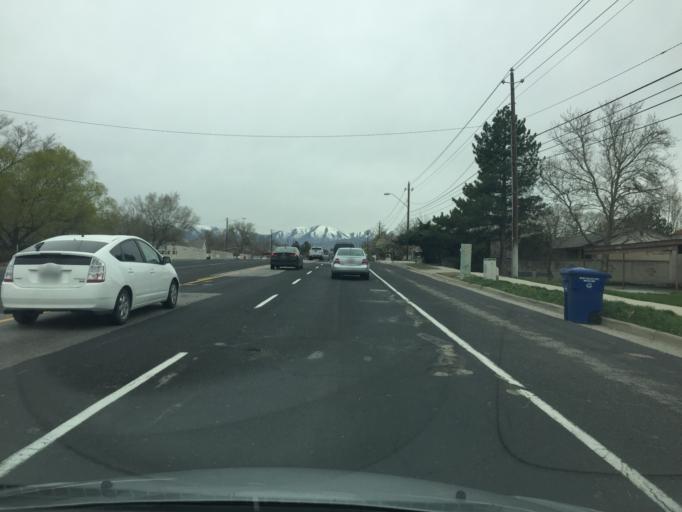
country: US
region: Utah
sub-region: Salt Lake County
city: Kearns
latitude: 40.6676
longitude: -111.9696
